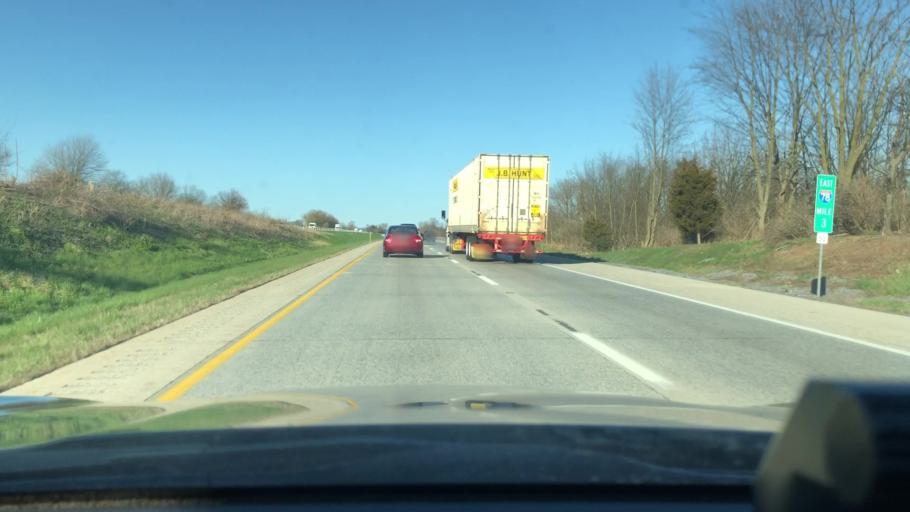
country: US
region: Pennsylvania
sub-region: Lebanon County
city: Jonestown
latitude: 40.4427
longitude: -76.4755
